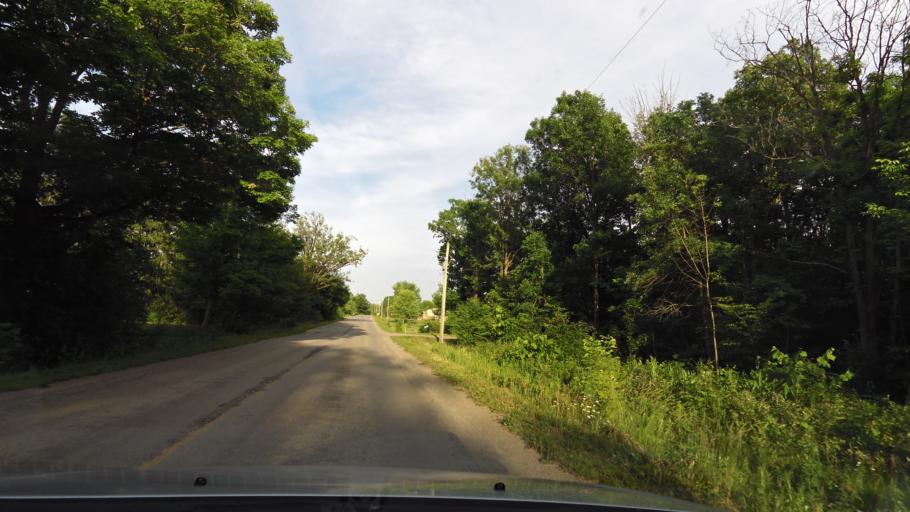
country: CA
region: Ontario
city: Ancaster
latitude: 43.0817
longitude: -80.0067
